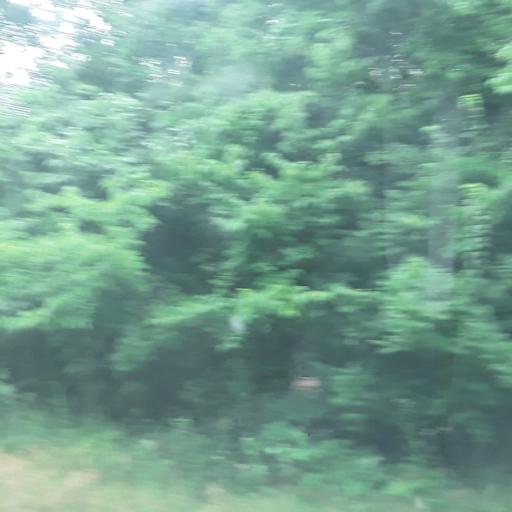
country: US
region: Tennessee
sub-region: Wilson County
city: Green Hill
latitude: 36.1609
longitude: -86.5971
